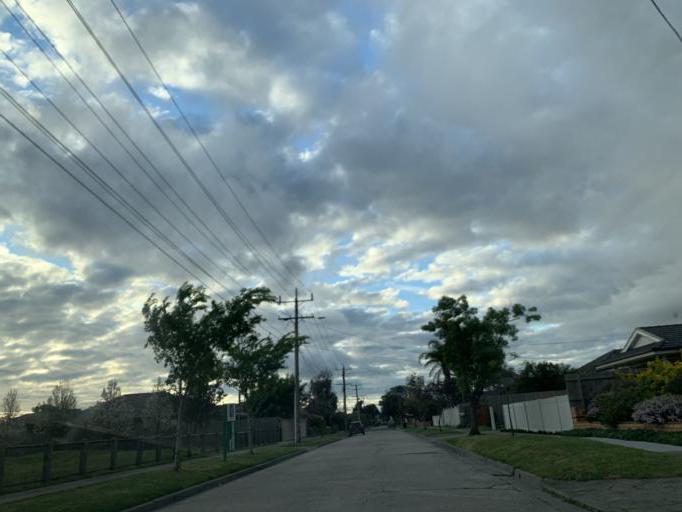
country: AU
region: Victoria
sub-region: Kingston
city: Aspendale
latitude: -38.0246
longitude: 145.1069
